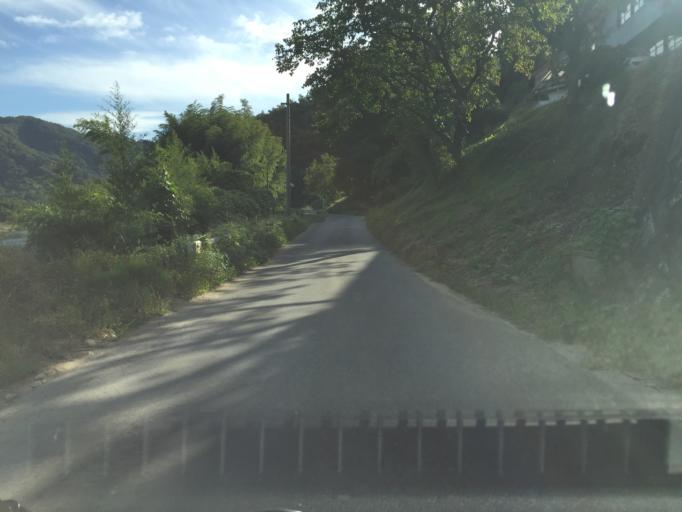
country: JP
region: Fukushima
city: Yanagawamachi-saiwaicho
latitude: 37.9103
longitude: 140.6620
